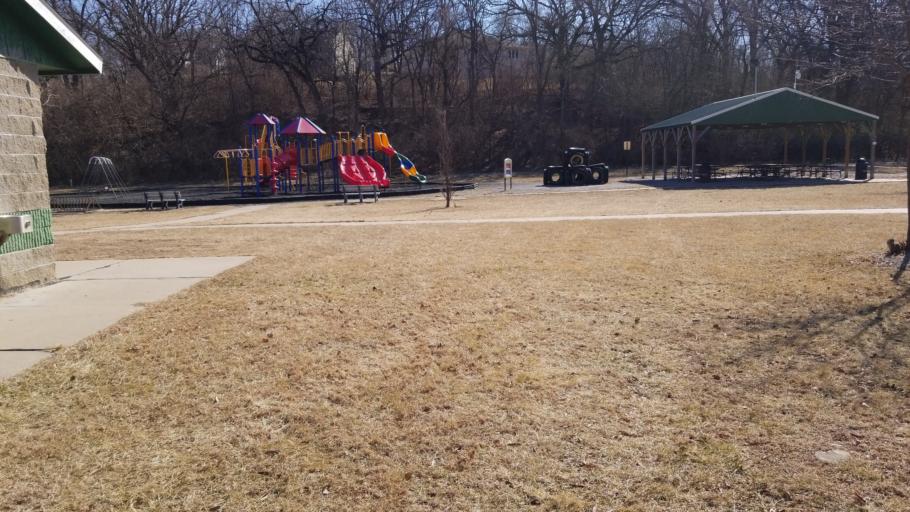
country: US
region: Nebraska
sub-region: Cass County
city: Plattsmouth
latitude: 41.0048
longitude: -95.8852
